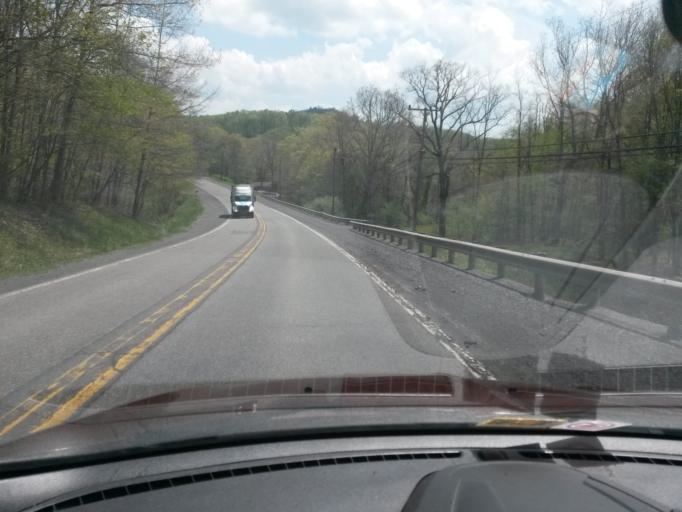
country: US
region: West Virginia
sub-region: Greenbrier County
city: Rainelle
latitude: 38.0366
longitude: -80.7305
